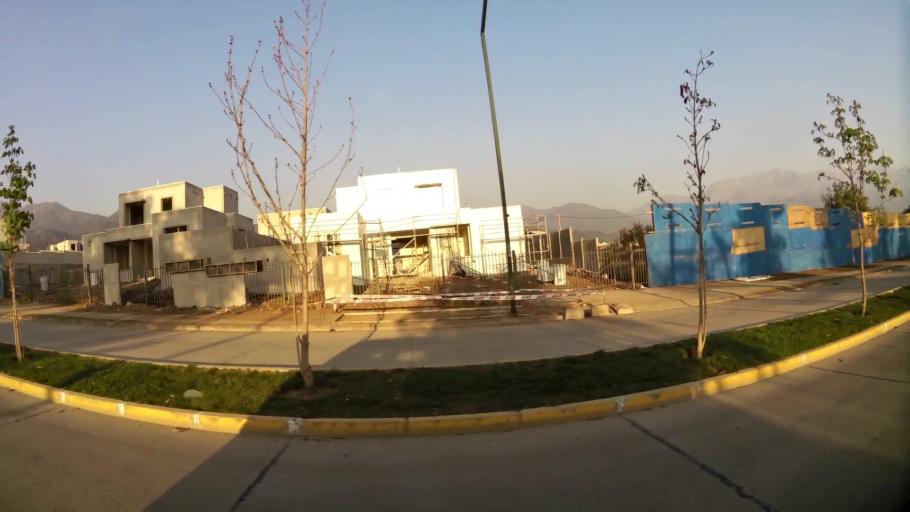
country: CL
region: Santiago Metropolitan
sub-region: Provincia de Chacabuco
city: Chicureo Abajo
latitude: -33.3235
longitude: -70.5189
